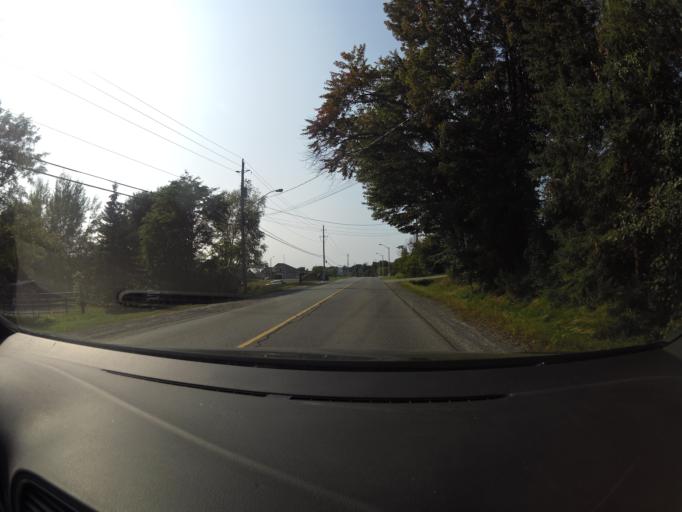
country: CA
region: Ontario
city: Bells Corners
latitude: 45.3440
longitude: -76.0193
